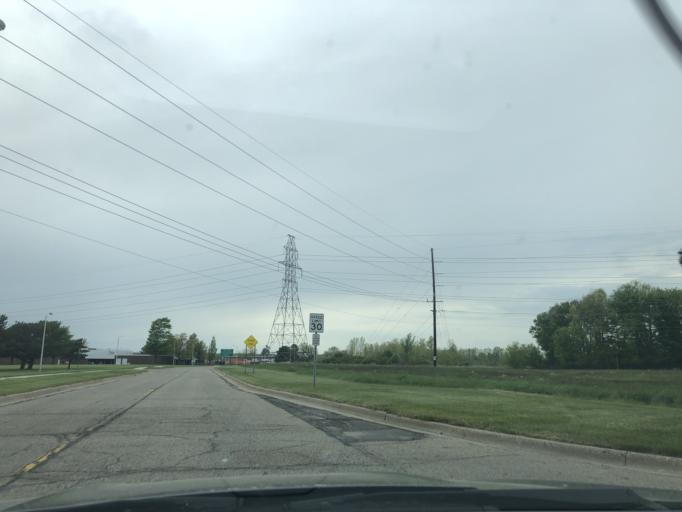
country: US
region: Michigan
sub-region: Eaton County
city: Dimondale
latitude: 42.6752
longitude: -84.6766
